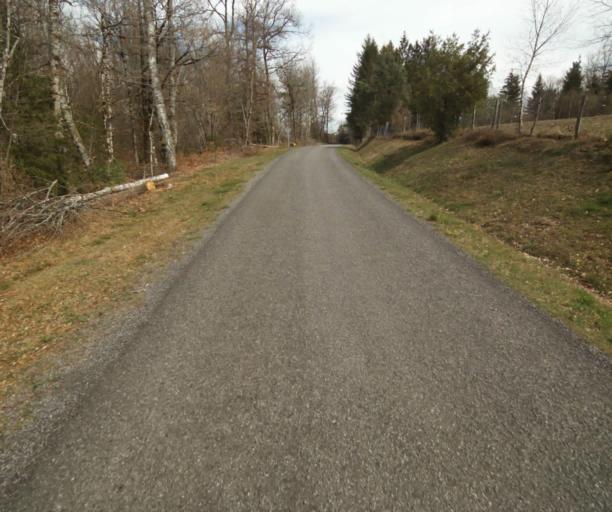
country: FR
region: Limousin
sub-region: Departement de la Correze
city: Correze
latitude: 45.3502
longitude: 1.9554
